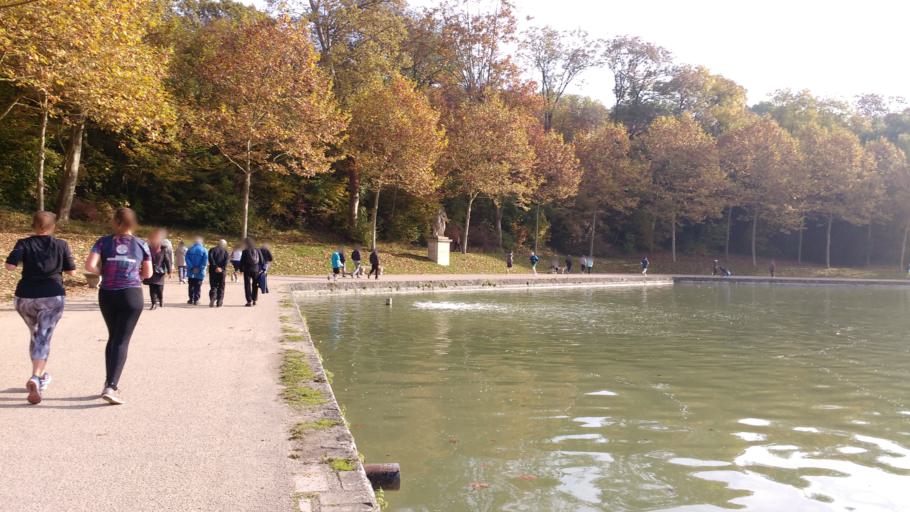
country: FR
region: Ile-de-France
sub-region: Departement des Hauts-de-Seine
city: Sceaux
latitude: 48.7693
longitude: 2.3016
